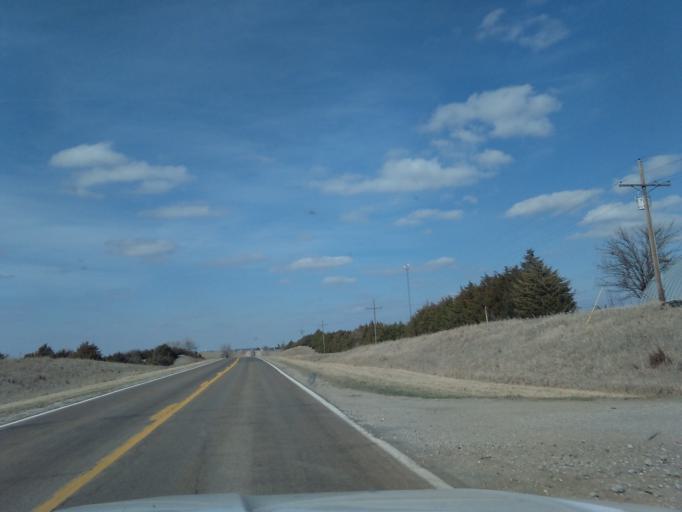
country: US
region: Nebraska
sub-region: Jefferson County
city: Fairbury
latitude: 40.0703
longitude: -96.9352
